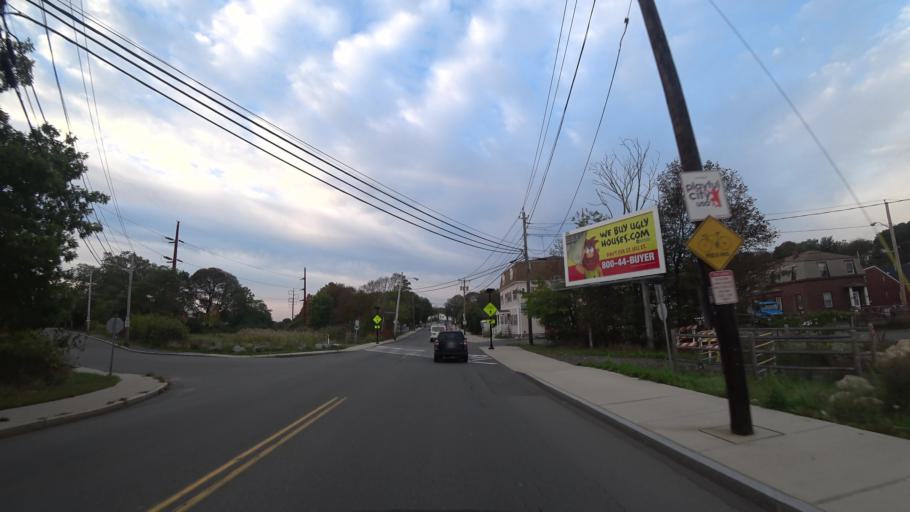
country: US
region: Massachusetts
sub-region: Essex County
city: Saugus
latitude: 42.4422
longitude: -71.0144
